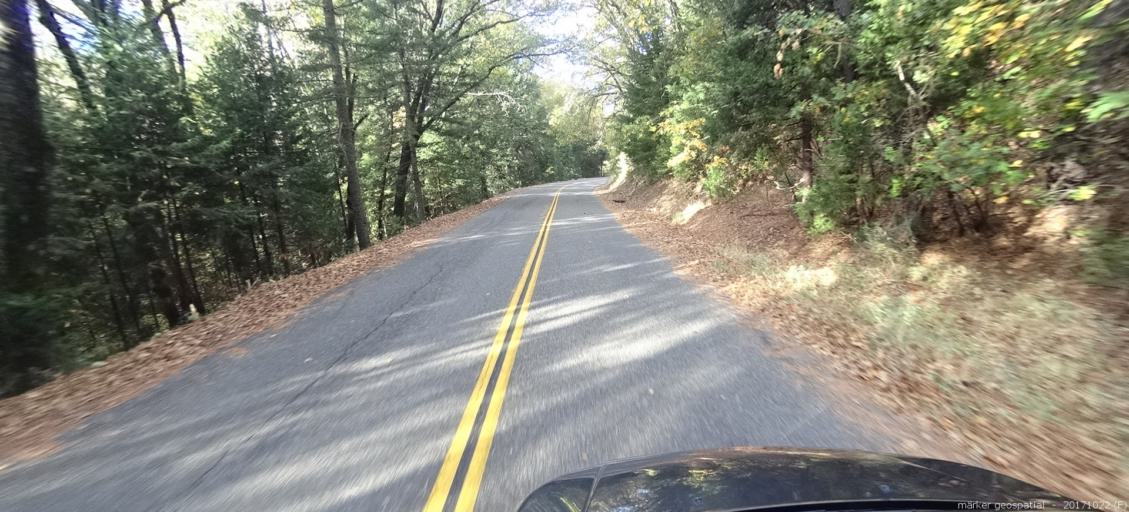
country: US
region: California
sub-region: Siskiyou County
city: Dunsmuir
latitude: 41.1509
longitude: -122.3016
